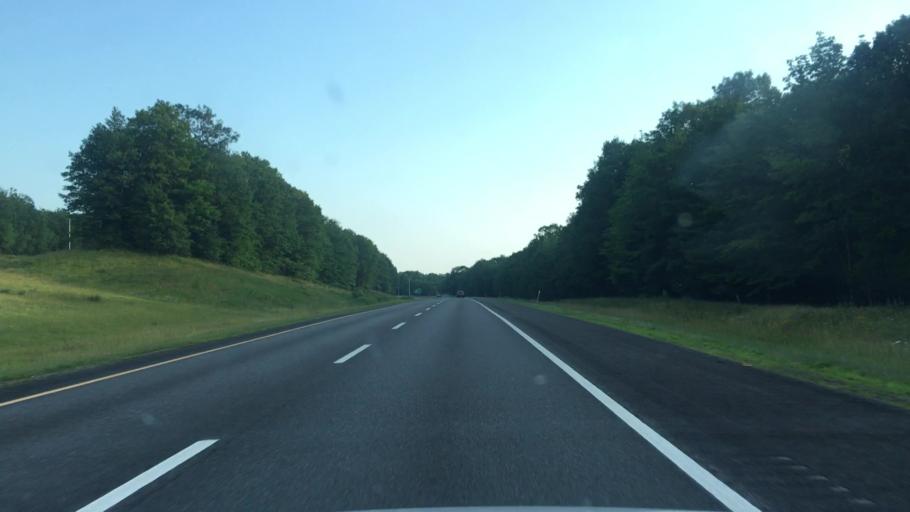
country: US
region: Maine
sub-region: Kennebec County
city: Gardiner
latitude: 44.1881
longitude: -69.8308
